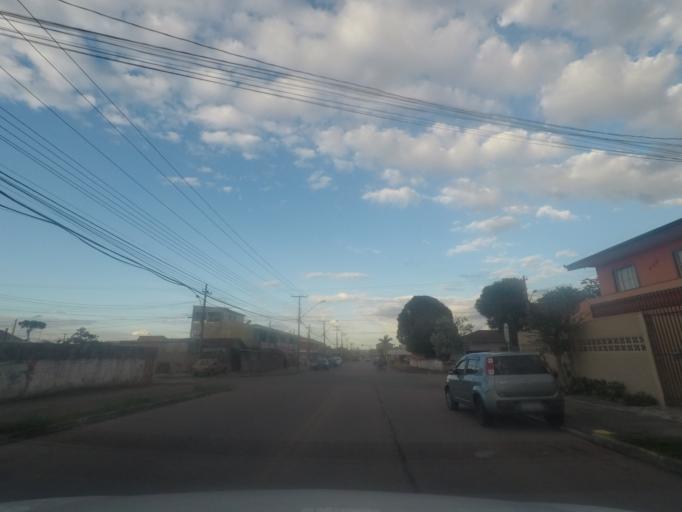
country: BR
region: Parana
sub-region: Pinhais
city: Pinhais
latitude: -25.4662
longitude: -49.2019
